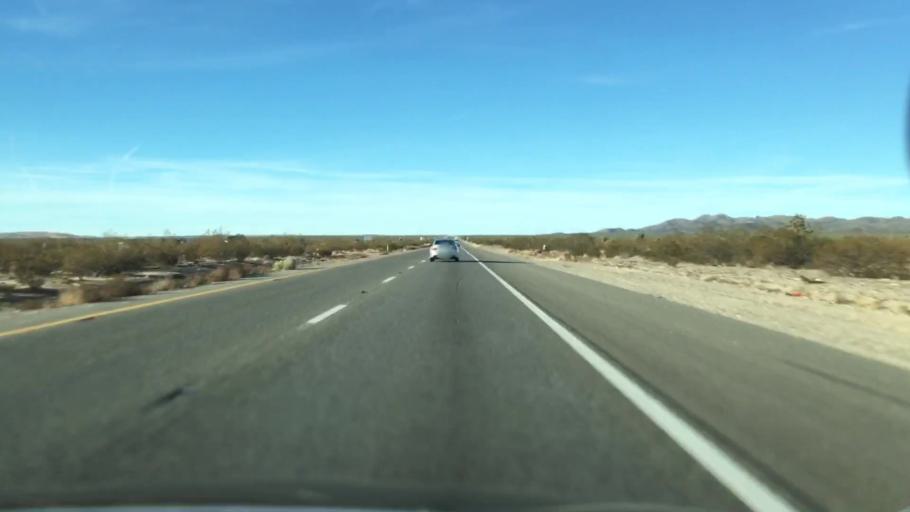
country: US
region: Nevada
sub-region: Clark County
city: Sandy Valley
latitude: 35.4243
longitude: -115.7310
